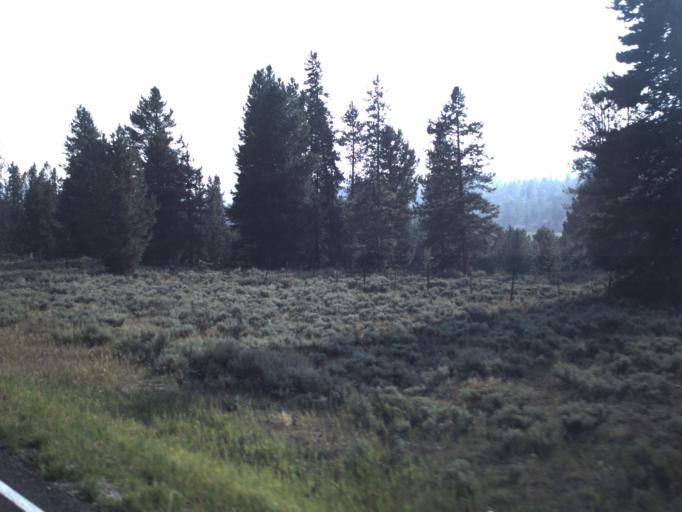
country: US
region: Wyoming
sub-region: Uinta County
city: Evanston
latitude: 40.8898
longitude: -110.8315
